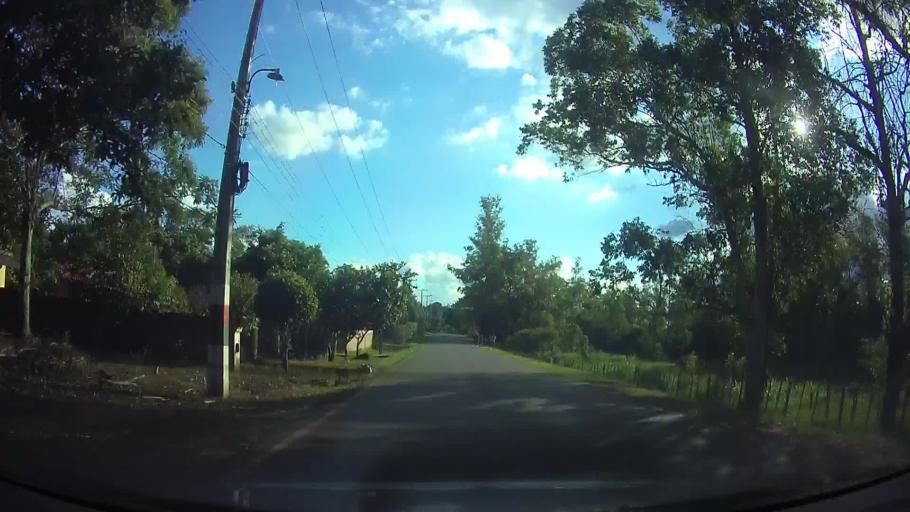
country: PY
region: Central
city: Aregua
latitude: -25.2664
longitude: -57.4247
